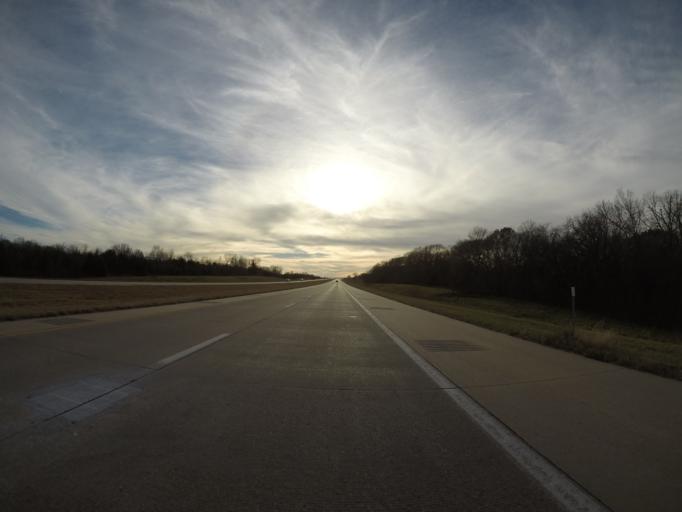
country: US
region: Kansas
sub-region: Franklin County
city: Ottawa
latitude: 38.5450
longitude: -95.3673
